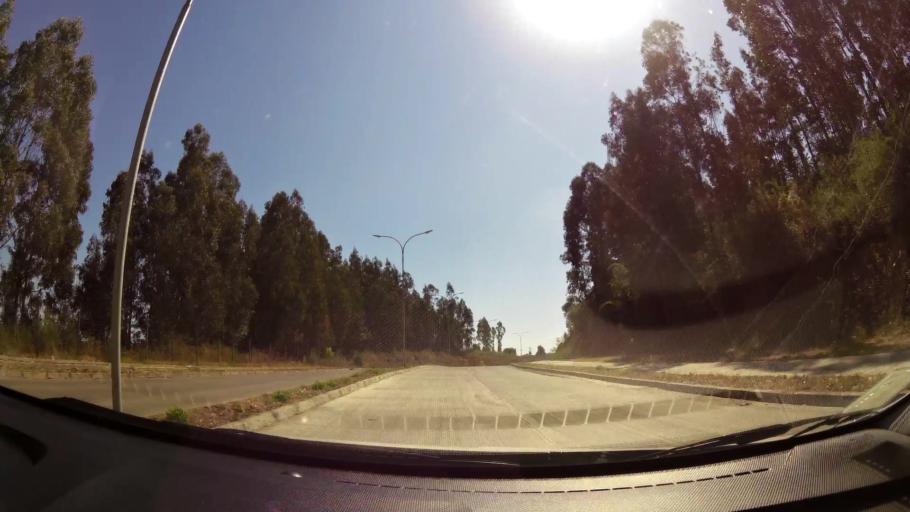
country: CL
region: Biobio
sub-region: Provincia de Concepcion
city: Concepcion
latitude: -36.7872
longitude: -73.0351
